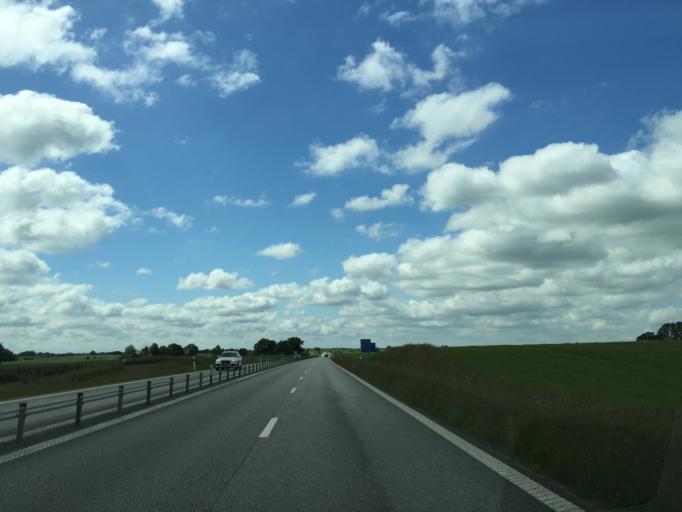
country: SE
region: Skane
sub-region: Skurups Kommun
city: Rydsgard
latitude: 55.4774
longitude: 13.6383
